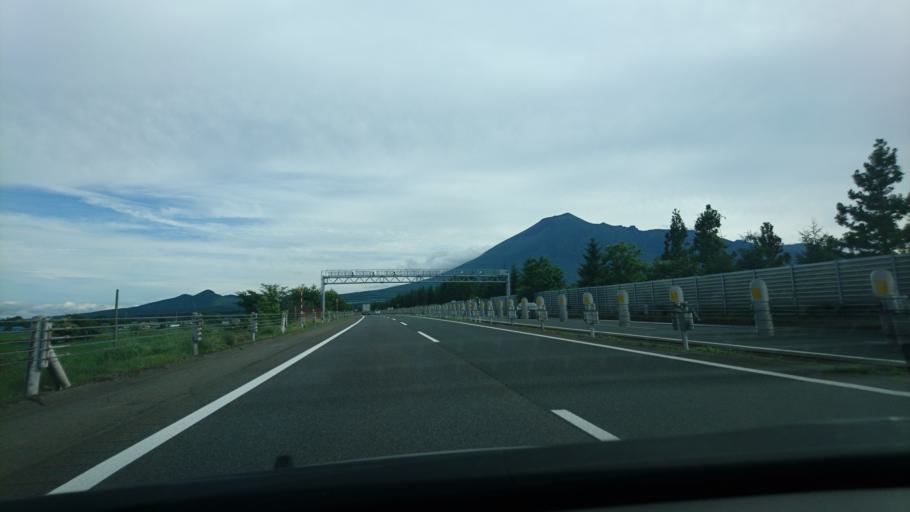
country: JP
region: Iwate
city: Shizukuishi
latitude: 39.9359
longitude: 141.0309
